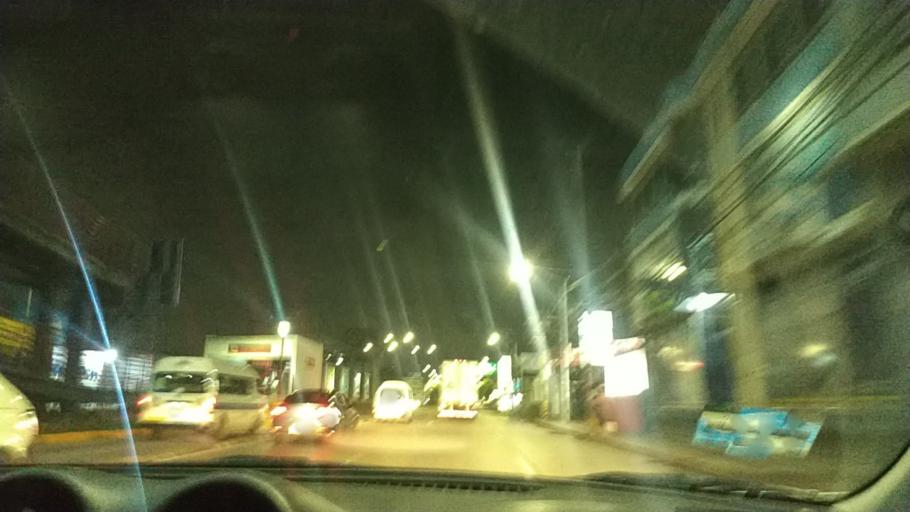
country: MX
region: Mexico
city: Coacalco
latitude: 19.6354
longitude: -99.1027
